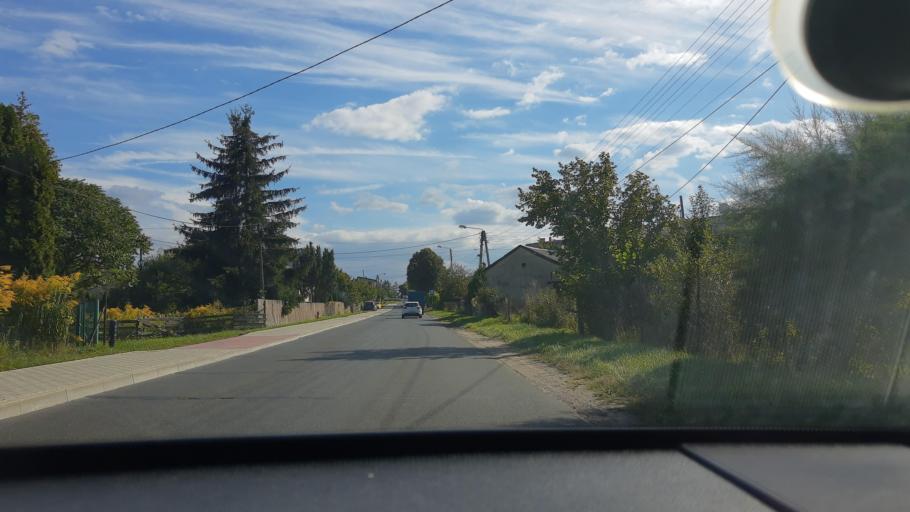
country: PL
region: Lodz Voivodeship
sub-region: Powiat sieradzki
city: Sieradz
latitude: 51.5803
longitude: 18.7371
